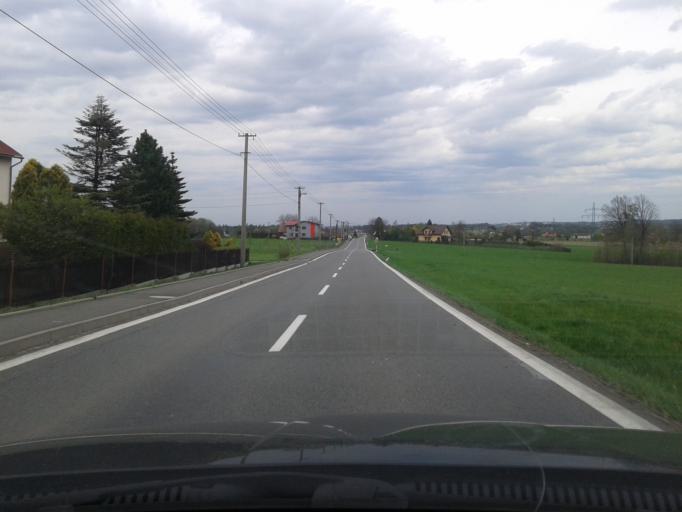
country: CZ
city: Sedliste
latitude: 49.7322
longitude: 18.3667
